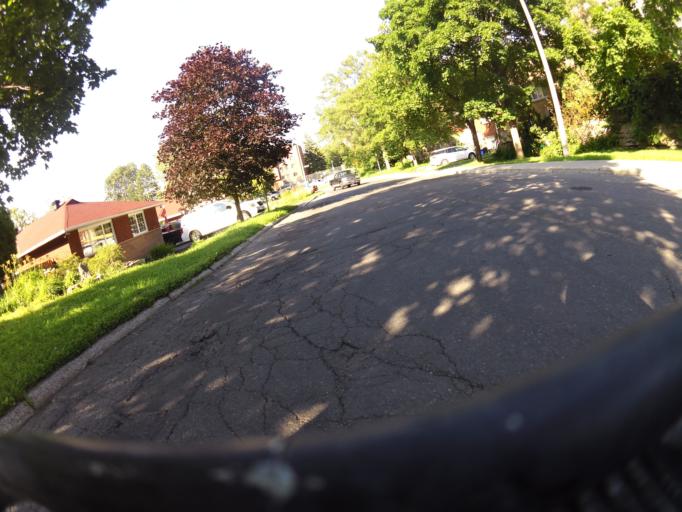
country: CA
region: Ontario
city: Ottawa
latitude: 45.3753
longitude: -75.7363
